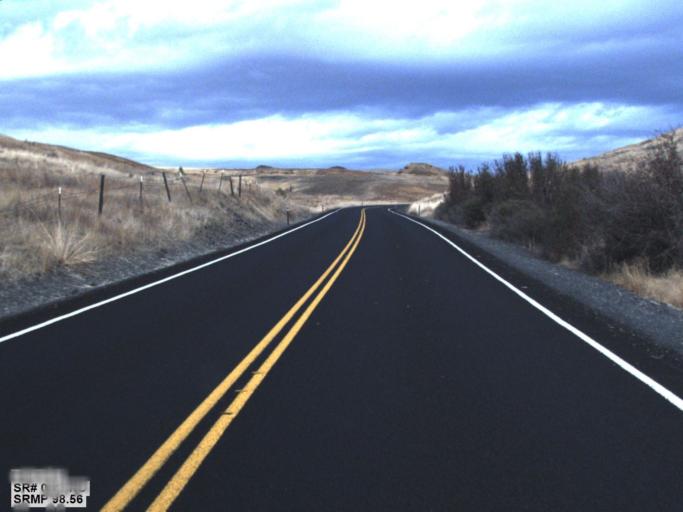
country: US
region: Washington
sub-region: Okanogan County
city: Coulee Dam
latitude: 47.8507
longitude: -118.7180
